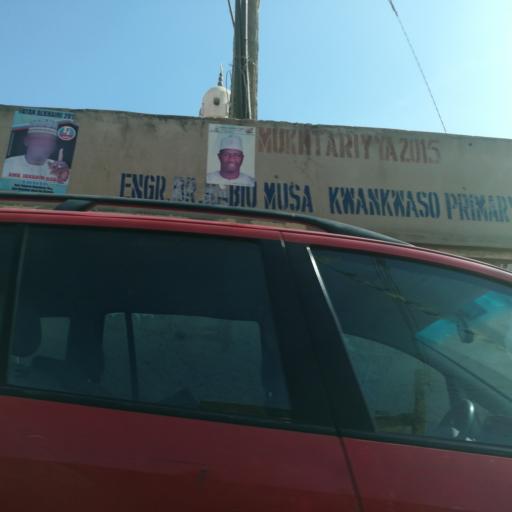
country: NG
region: Kano
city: Kano
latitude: 12.0052
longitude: 8.5182
